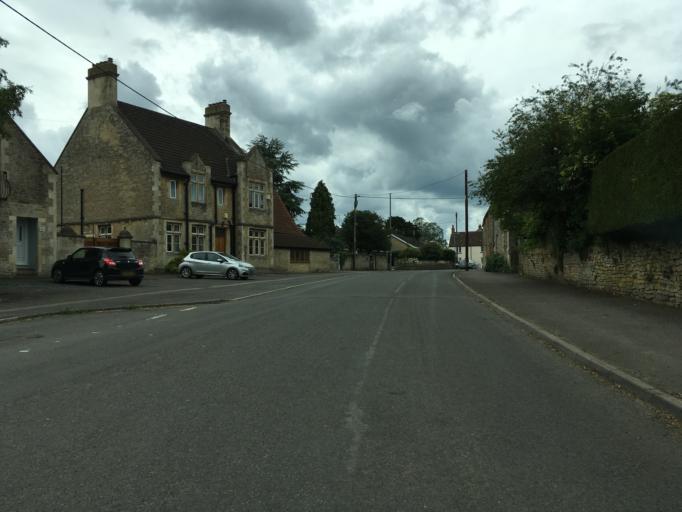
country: GB
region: England
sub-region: Wiltshire
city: Norton
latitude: 51.5381
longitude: -2.1516
